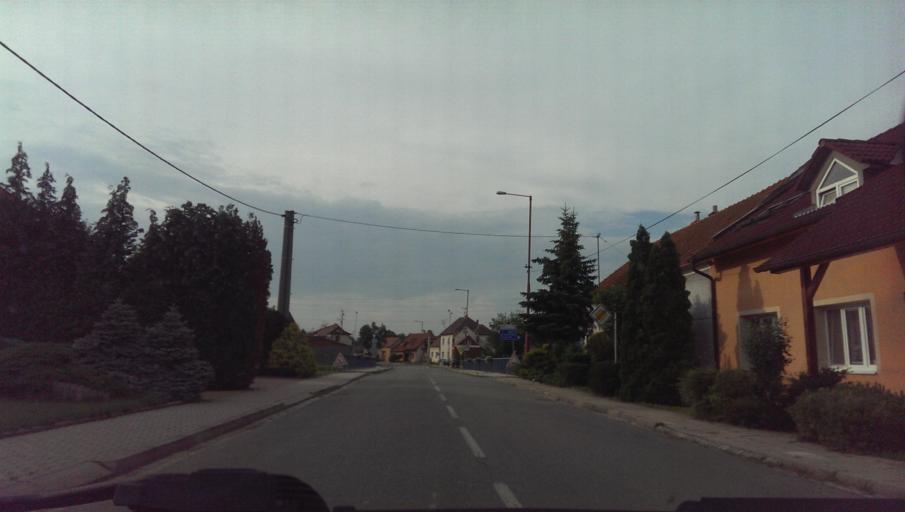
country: CZ
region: Zlin
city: Popovice
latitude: 49.0403
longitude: 17.5028
